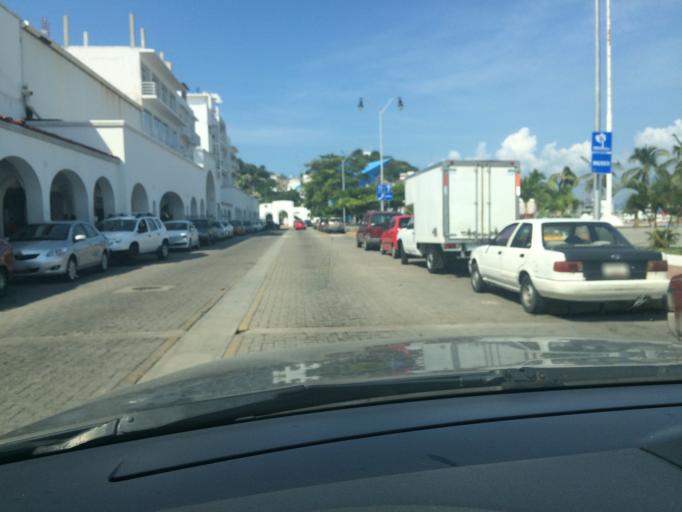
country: MX
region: Colima
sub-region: Manzanillo
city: Manzanillo
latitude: 19.0536
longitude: -104.3149
